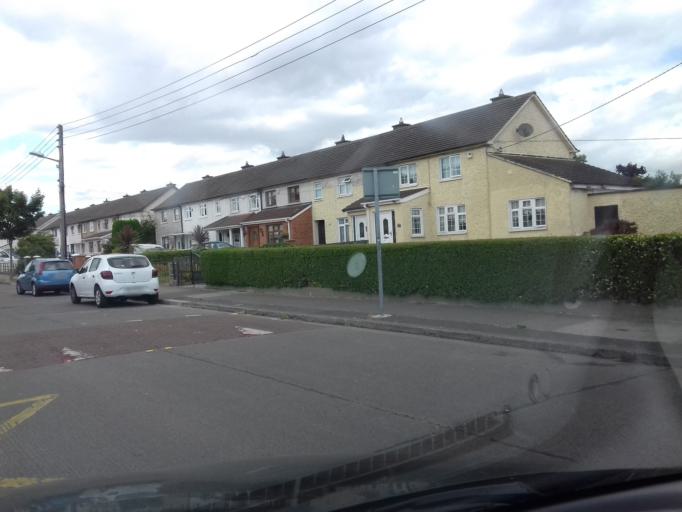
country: IE
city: Bonnybrook
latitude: 53.3987
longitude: -6.2033
